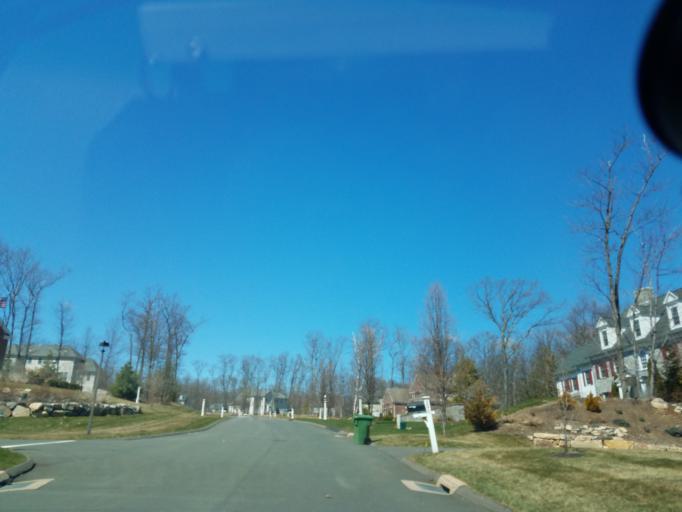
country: US
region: Connecticut
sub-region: Hartford County
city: Collinsville
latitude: 41.8033
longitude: -72.9000
